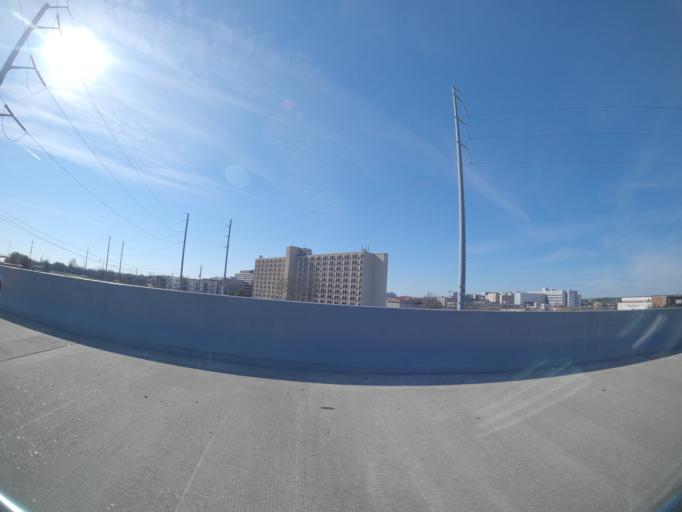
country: US
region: Georgia
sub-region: Richmond County
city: Augusta
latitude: 33.4762
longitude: -81.9822
